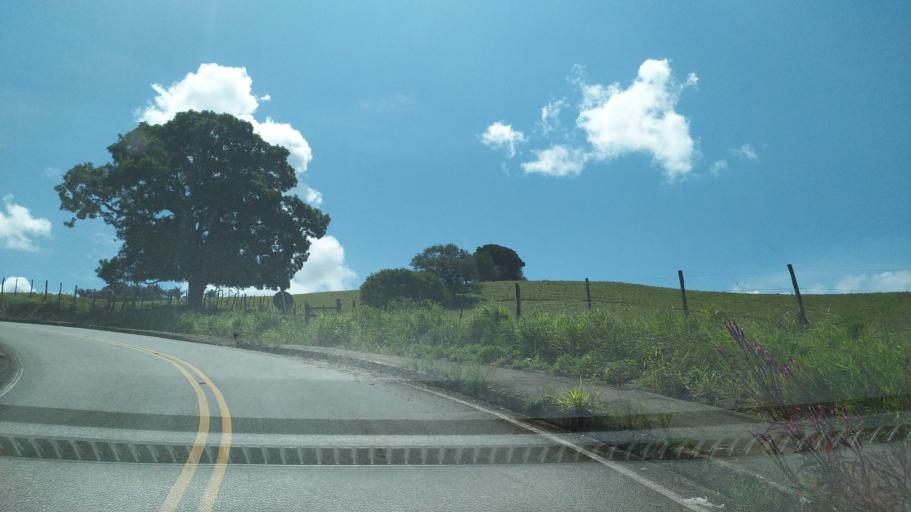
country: BR
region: Alagoas
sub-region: Uniao Dos Palmares
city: Uniao dos Palmares
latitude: -9.1630
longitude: -36.0681
